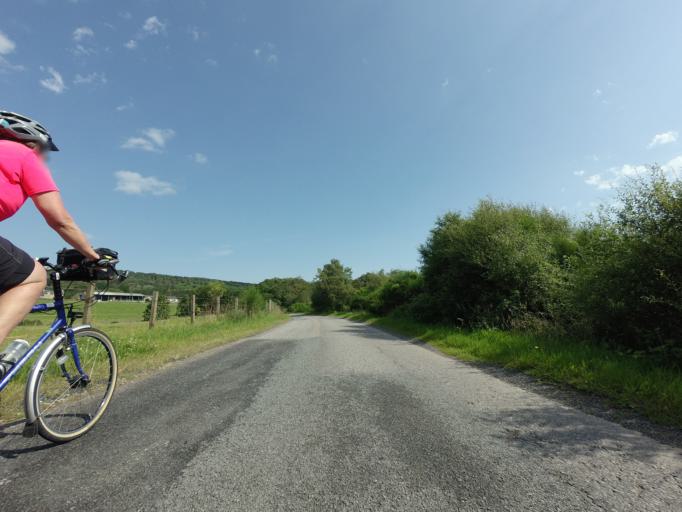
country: GB
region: Scotland
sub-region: Highland
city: Invergordon
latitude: 57.7505
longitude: -4.1605
